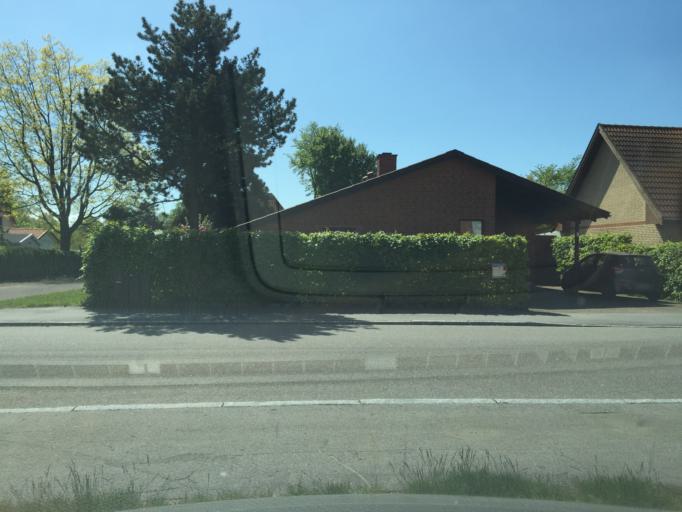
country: DK
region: Zealand
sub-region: Vordingborg Kommune
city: Stege
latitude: 54.9900
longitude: 12.2917
